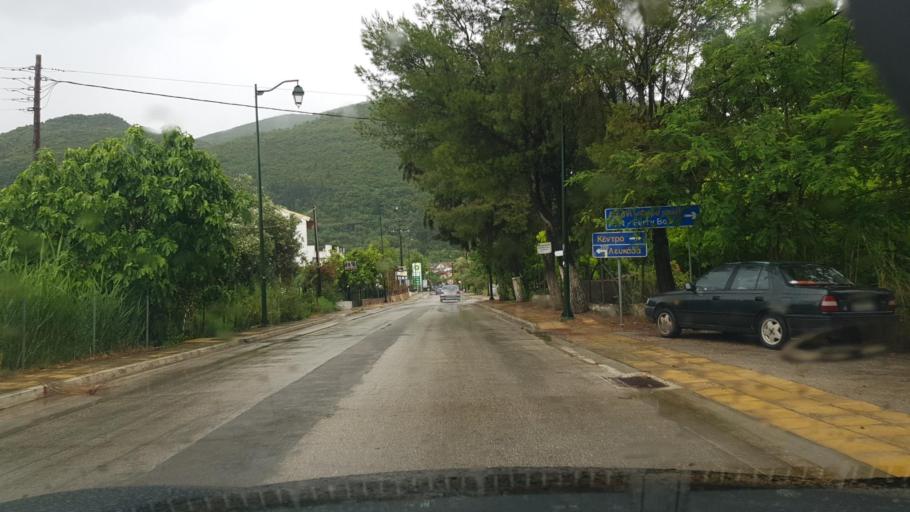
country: GR
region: Ionian Islands
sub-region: Lefkada
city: Nidri
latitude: 38.6311
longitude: 20.6068
